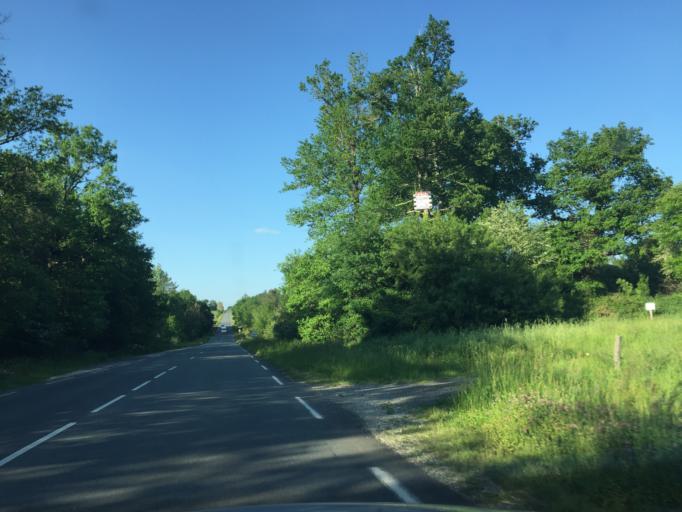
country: FR
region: Aquitaine
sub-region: Departement de la Dordogne
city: La Roche-Chalais
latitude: 45.1773
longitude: 0.0212
